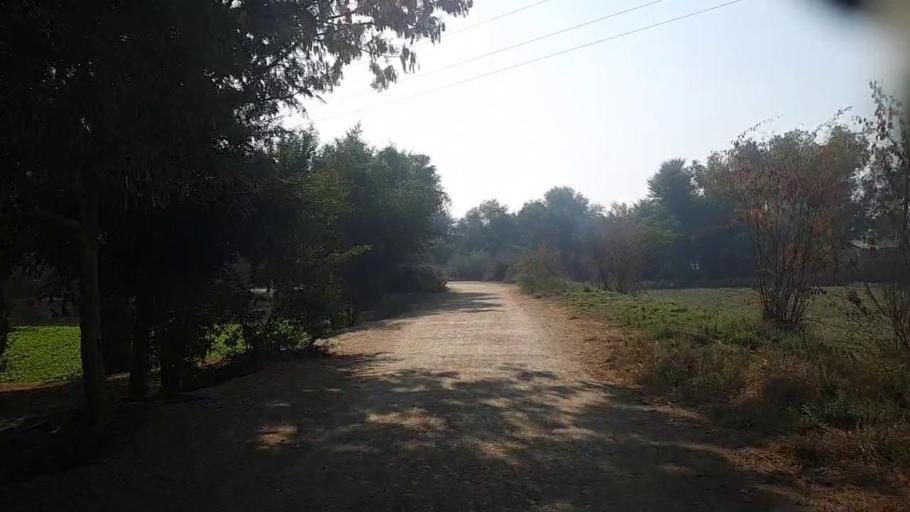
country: PK
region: Sindh
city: Kandiari
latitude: 27.0253
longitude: 68.5058
